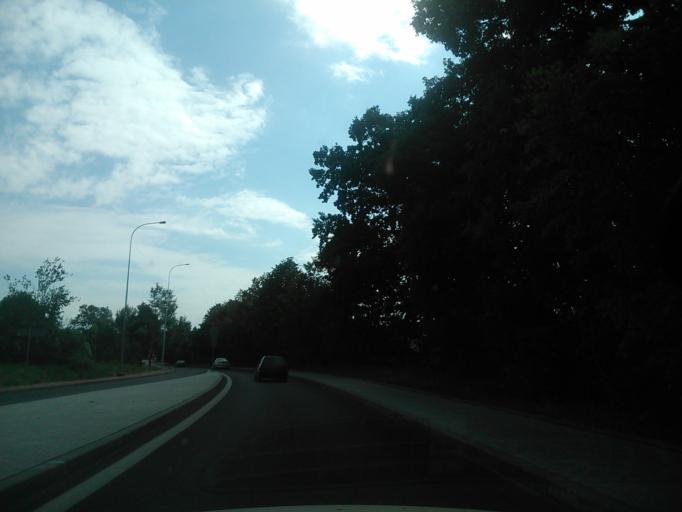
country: PL
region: Warmian-Masurian Voivodeship
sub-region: Powiat dzialdowski
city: Ilowo -Osada
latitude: 53.1631
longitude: 20.2965
